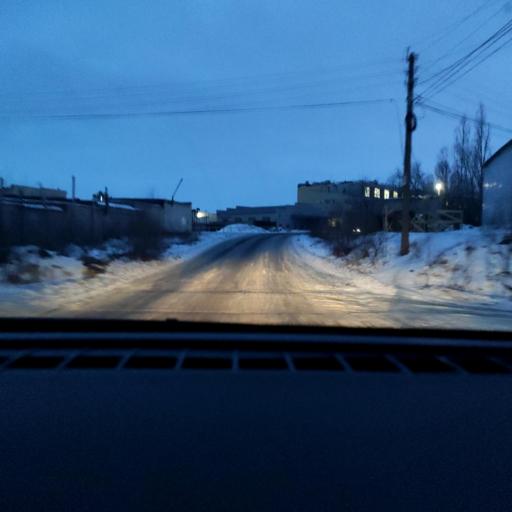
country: RU
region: Voronezj
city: Somovo
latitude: 51.7121
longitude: 39.2854
